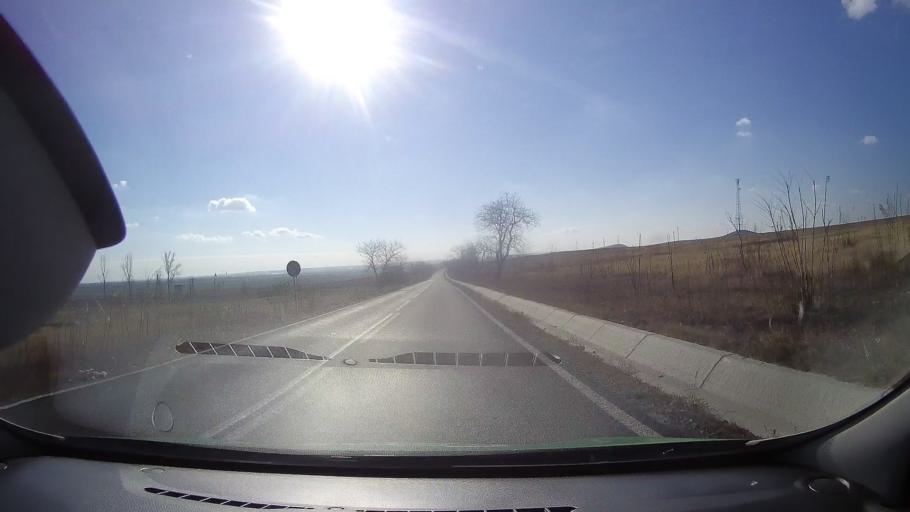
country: RO
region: Tulcea
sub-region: Comuna Ceamurlia de Jos
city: Ceamurlia de Jos
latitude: 44.8118
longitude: 28.6915
